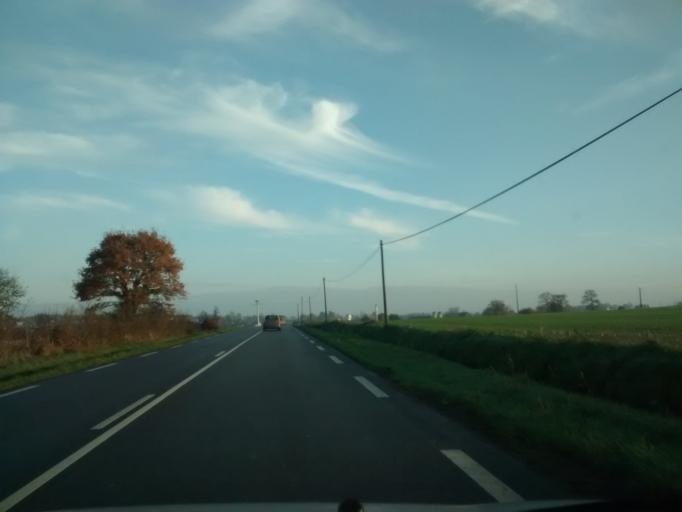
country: FR
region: Brittany
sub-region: Departement d'Ille-et-Vilaine
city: Tremblay
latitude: 48.4126
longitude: -1.4785
